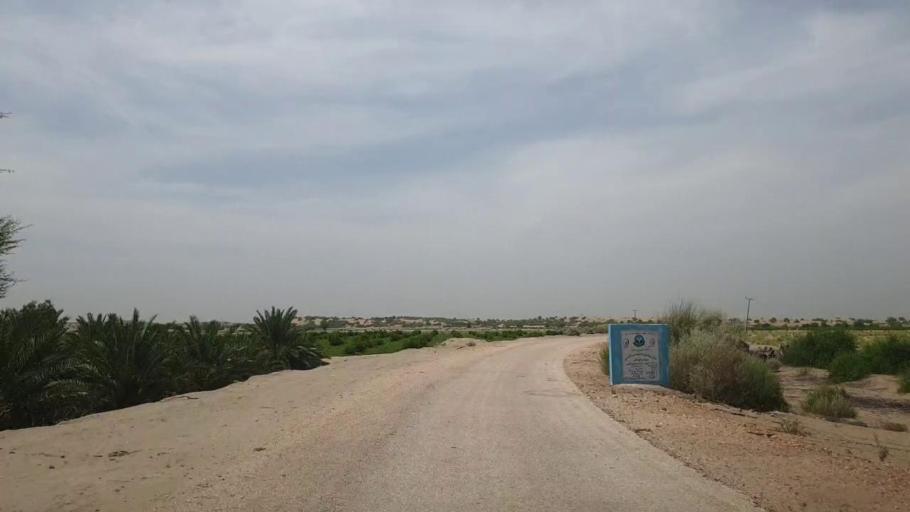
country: PK
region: Sindh
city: Kot Diji
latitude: 27.0858
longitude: 69.0739
